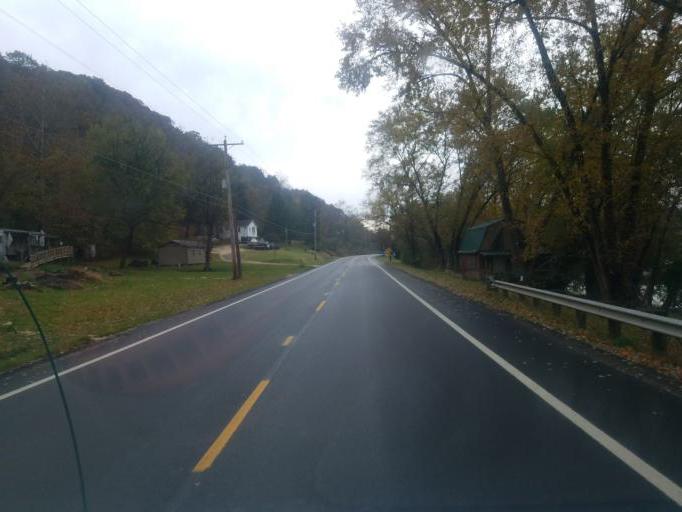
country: US
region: Ohio
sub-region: Washington County
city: Beverly
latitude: 39.5630
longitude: -81.5699
